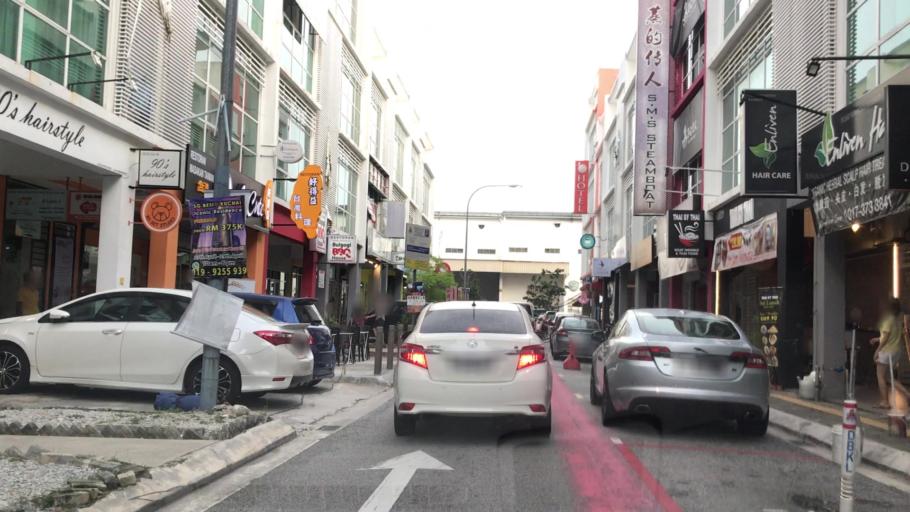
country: MY
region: Selangor
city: Kampong Baharu Balakong
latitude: 3.0709
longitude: 101.6926
